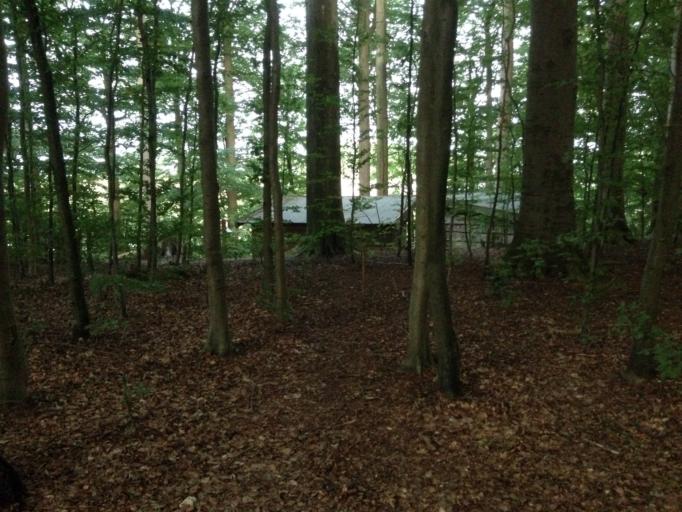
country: DK
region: South Denmark
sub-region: Sonderborg Kommune
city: Horuphav
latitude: 54.9026
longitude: 9.8753
